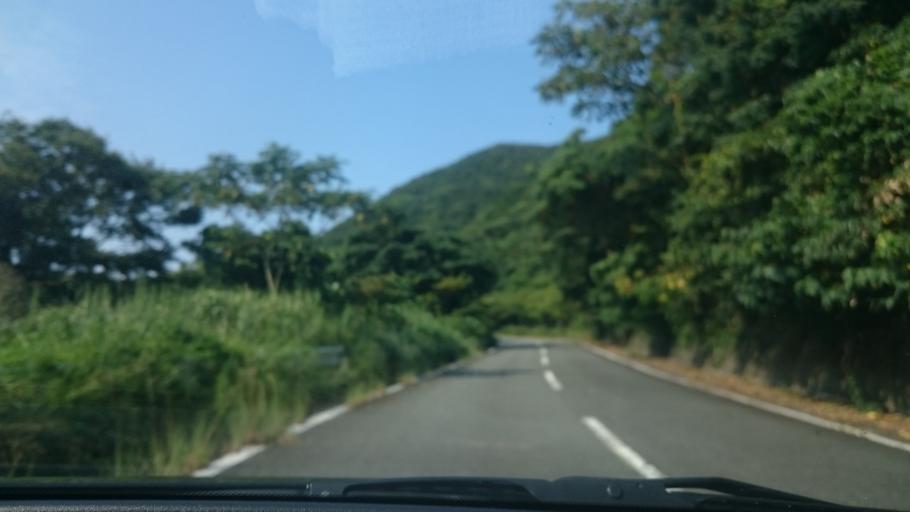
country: JP
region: Shizuoka
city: Heda
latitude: 35.0054
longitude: 138.7808
